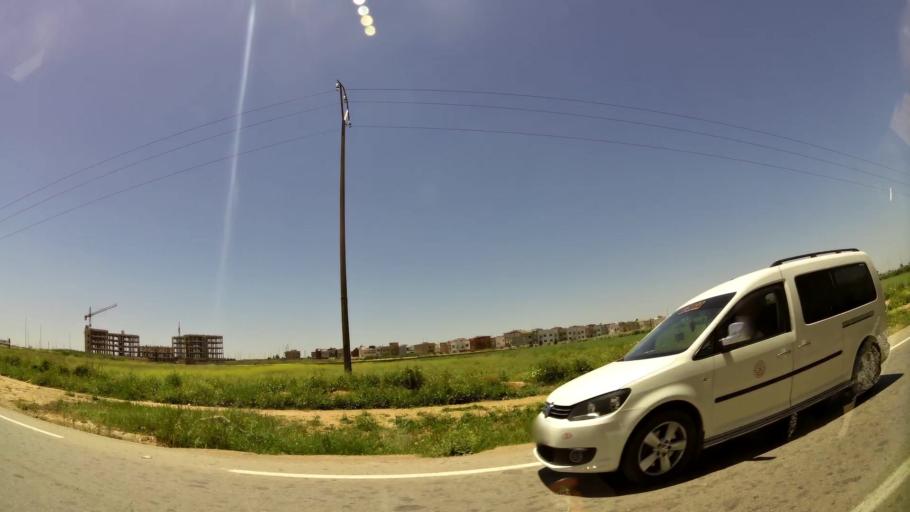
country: MA
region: Meknes-Tafilalet
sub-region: Meknes
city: Meknes
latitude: 33.8541
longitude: -5.5694
